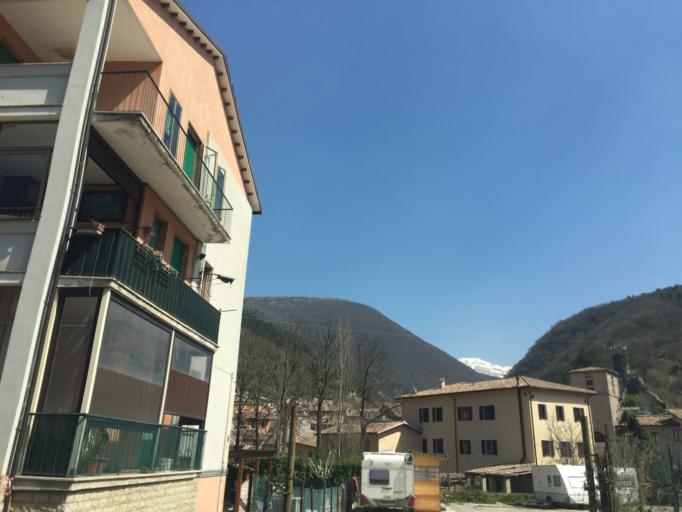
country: IT
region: The Marches
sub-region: Provincia di Macerata
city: Visso
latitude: 42.9299
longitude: 13.0867
